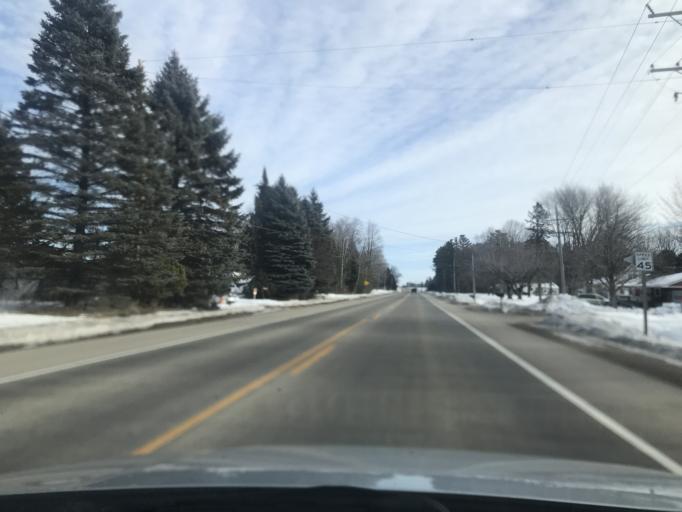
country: US
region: Wisconsin
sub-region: Oconto County
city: Gillett
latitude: 44.8966
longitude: -88.2903
